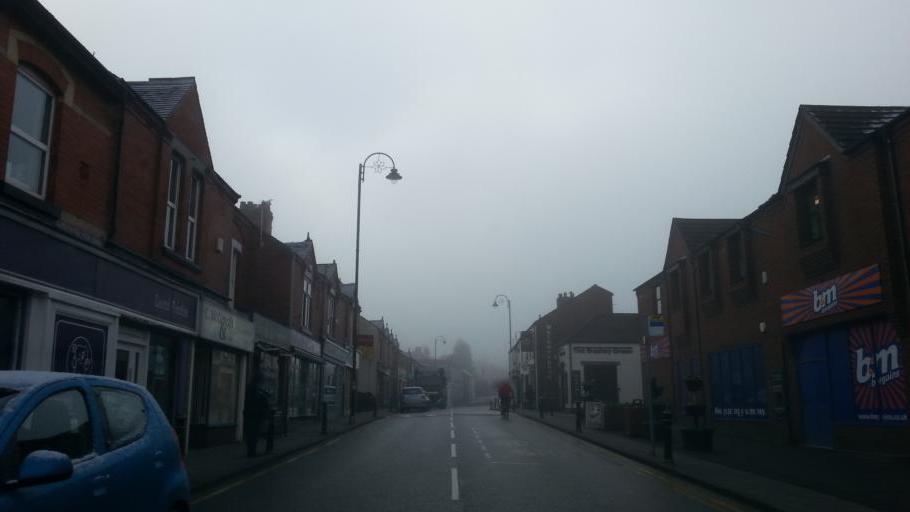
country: GB
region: England
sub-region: Staffordshire
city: Biddulph
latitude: 53.1162
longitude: -2.1760
